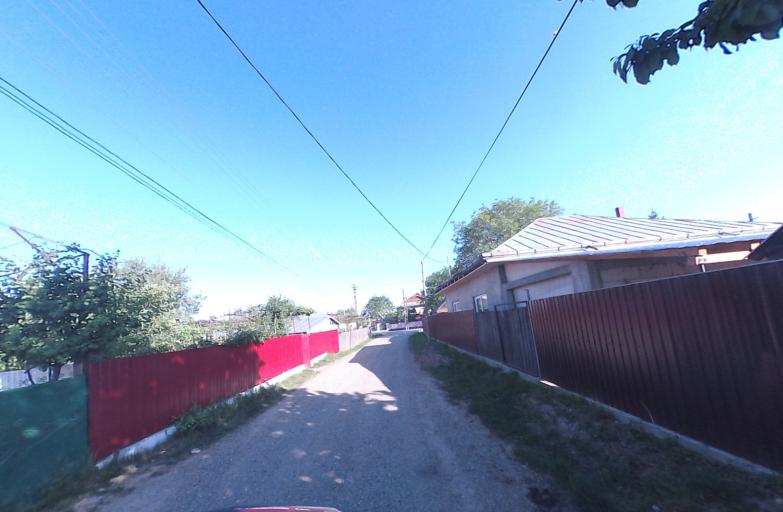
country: RO
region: Neamt
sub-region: Comuna Cordun
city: Pildesti
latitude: 46.9803
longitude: 26.8071
